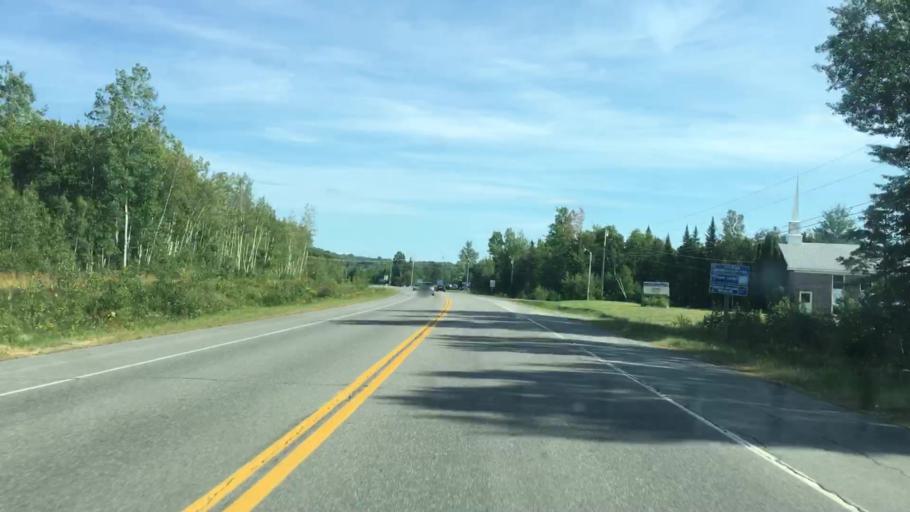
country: US
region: Maine
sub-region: Penobscot County
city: Lincoln
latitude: 45.3586
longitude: -68.5430
